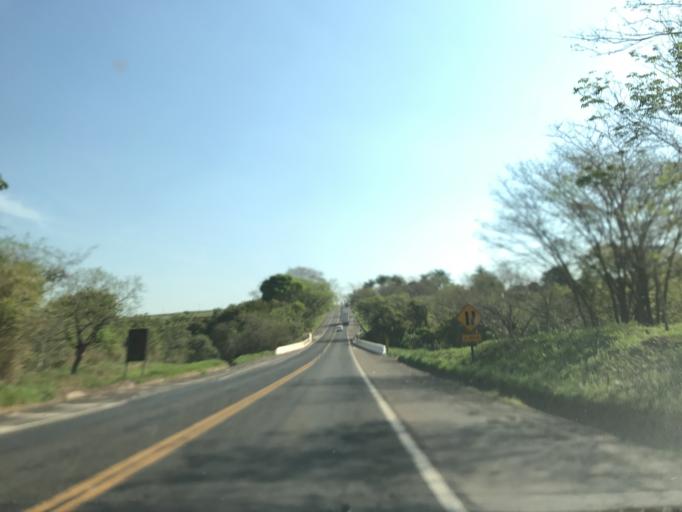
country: BR
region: Sao Paulo
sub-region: Penapolis
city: Penapolis
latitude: -21.4581
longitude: -50.1708
